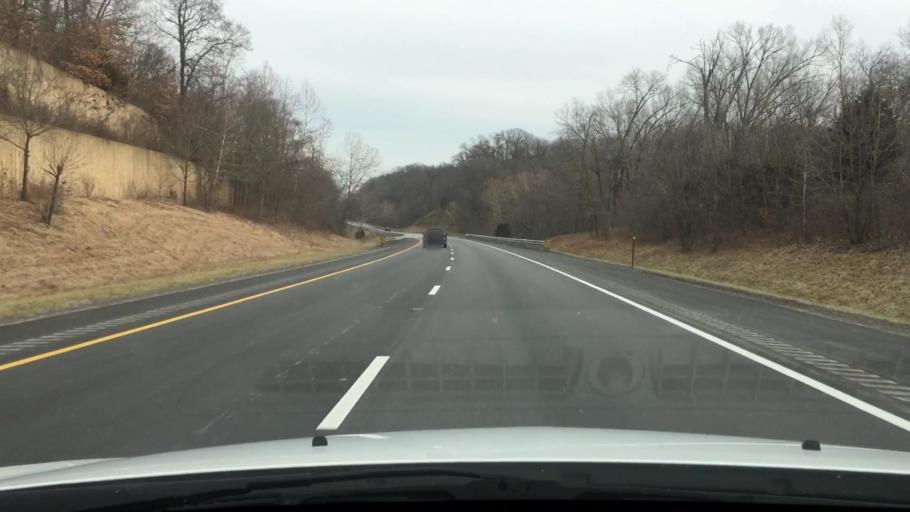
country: US
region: Illinois
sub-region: Pike County
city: Griggsville
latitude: 39.6815
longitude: -90.6557
